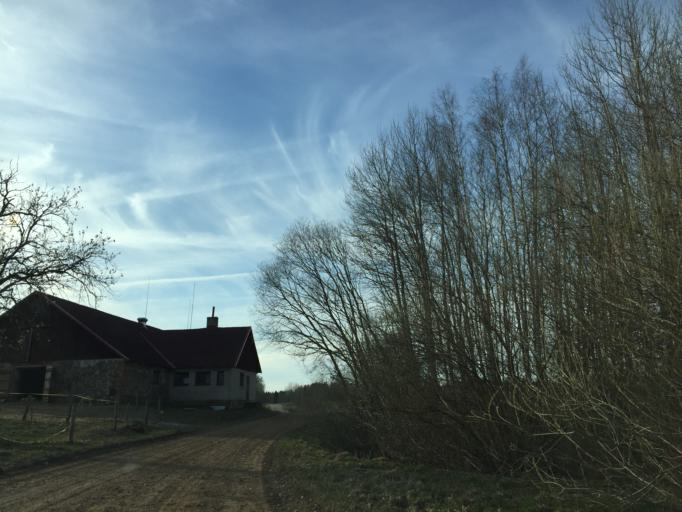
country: EE
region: Tartu
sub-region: Noo vald
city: Noo
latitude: 58.1337
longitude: 26.5954
